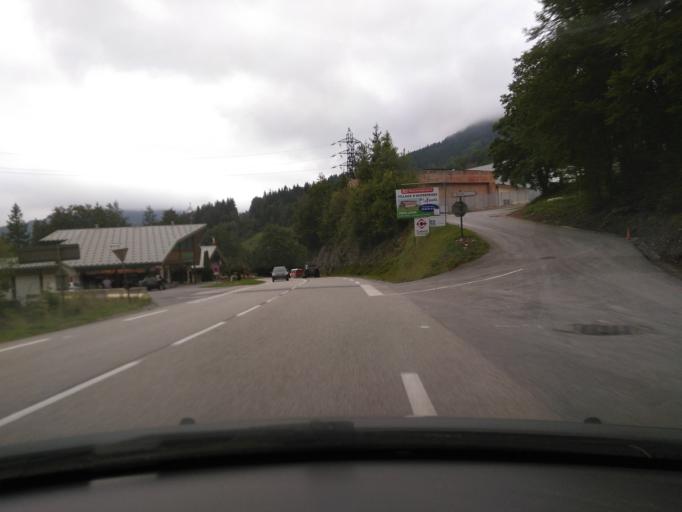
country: FR
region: Rhone-Alpes
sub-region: Departement de la Haute-Savoie
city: La Clusaz
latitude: 45.9138
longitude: 6.4182
